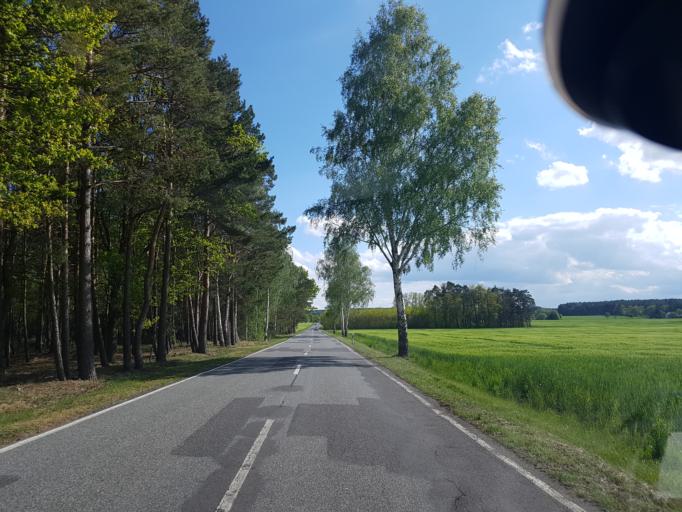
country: DE
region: Brandenburg
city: Drebkau
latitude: 51.6468
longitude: 14.2784
